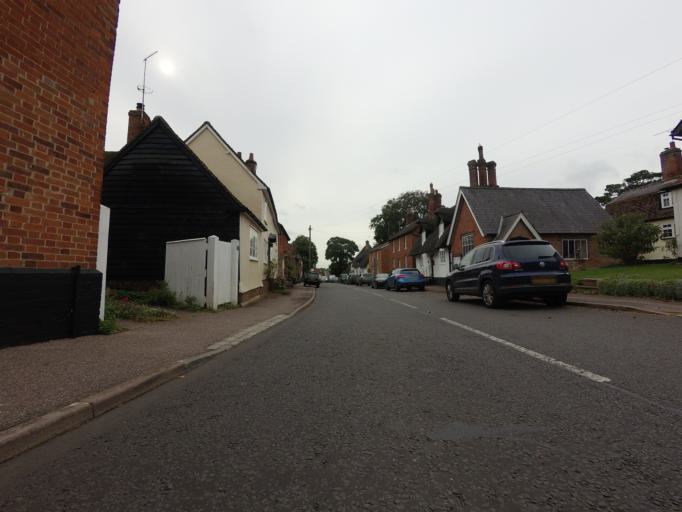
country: GB
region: England
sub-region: Hertfordshire
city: Reed
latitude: 52.0044
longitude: 0.0161
